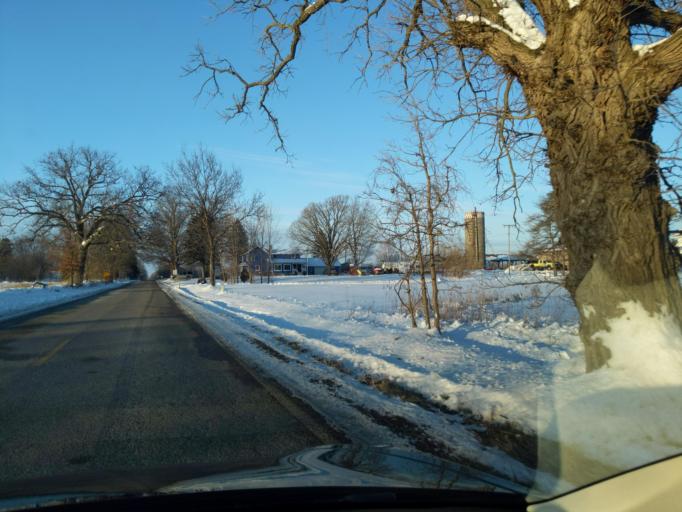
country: US
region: Michigan
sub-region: Ingham County
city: Stockbridge
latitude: 42.5377
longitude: -84.1125
